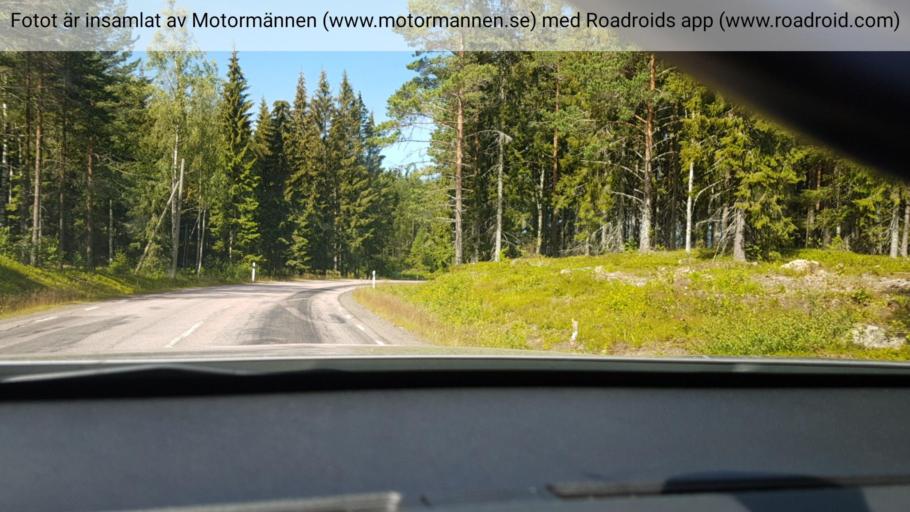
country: SE
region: Vaermland
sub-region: Sunne Kommun
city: Sunne
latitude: 59.8633
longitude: 13.2926
